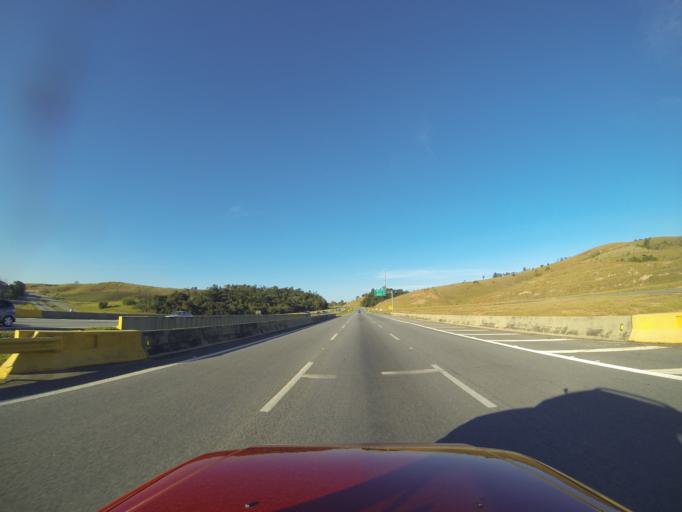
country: BR
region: Sao Paulo
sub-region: Jacarei
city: Jacarei
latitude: -23.3306
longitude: -45.9252
